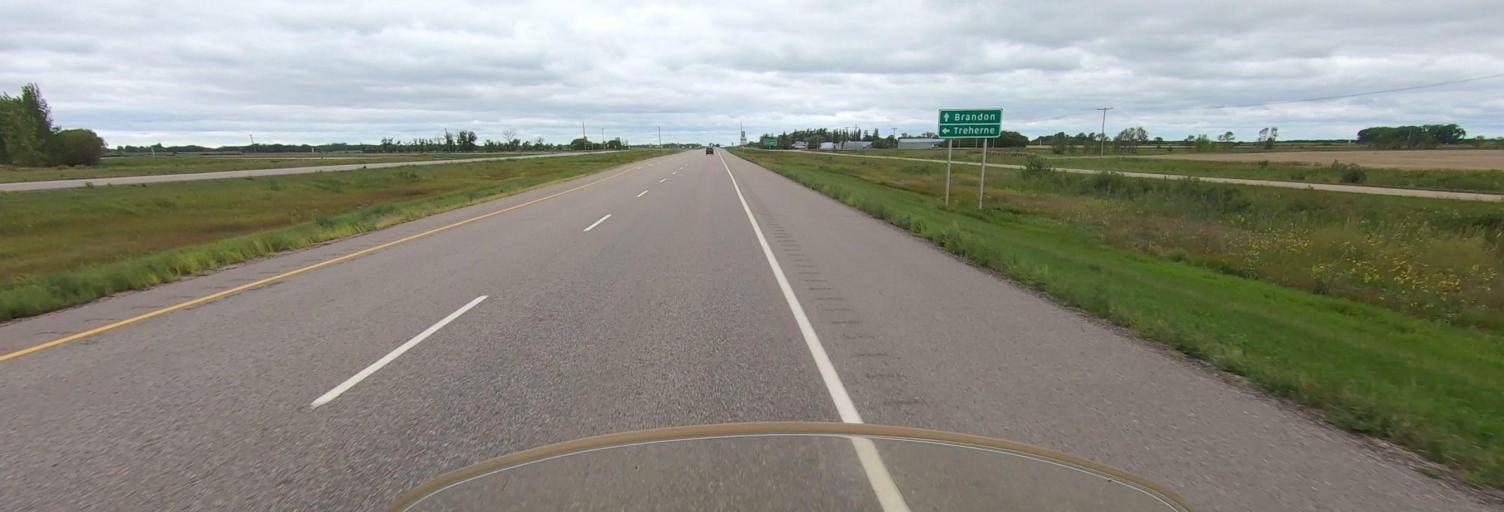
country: CA
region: Manitoba
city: Portage la Prairie
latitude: 49.9752
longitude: -98.6235
